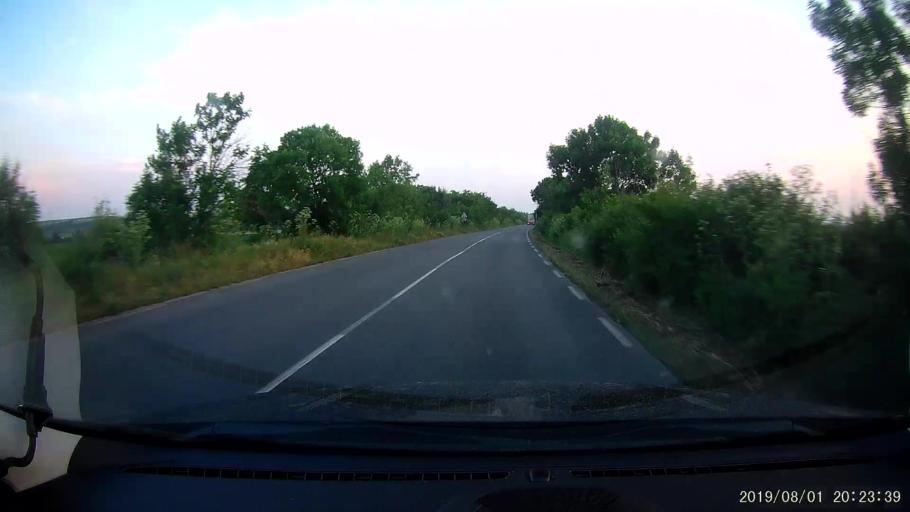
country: BG
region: Yambol
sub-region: Obshtina Elkhovo
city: Elkhovo
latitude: 42.2447
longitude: 26.5988
